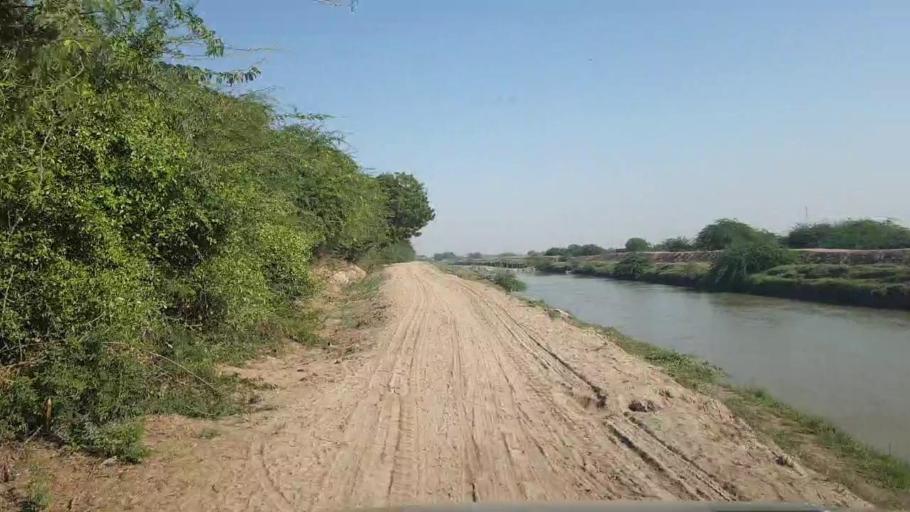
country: PK
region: Sindh
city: Badin
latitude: 24.7246
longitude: 68.8032
